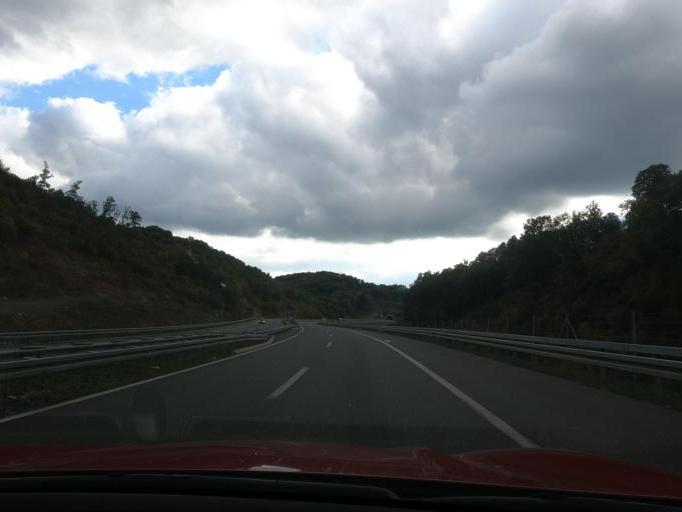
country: RS
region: Central Serbia
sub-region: Moravicki Okrug
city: Gornji Milanovac
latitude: 44.0334
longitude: 20.3657
